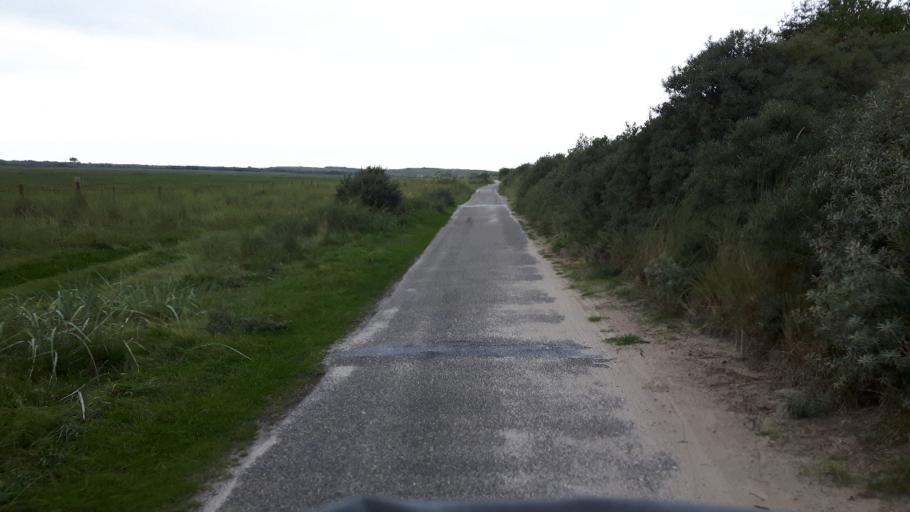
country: NL
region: Friesland
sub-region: Gemeente Ameland
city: Nes
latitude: 53.4611
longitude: 5.8477
